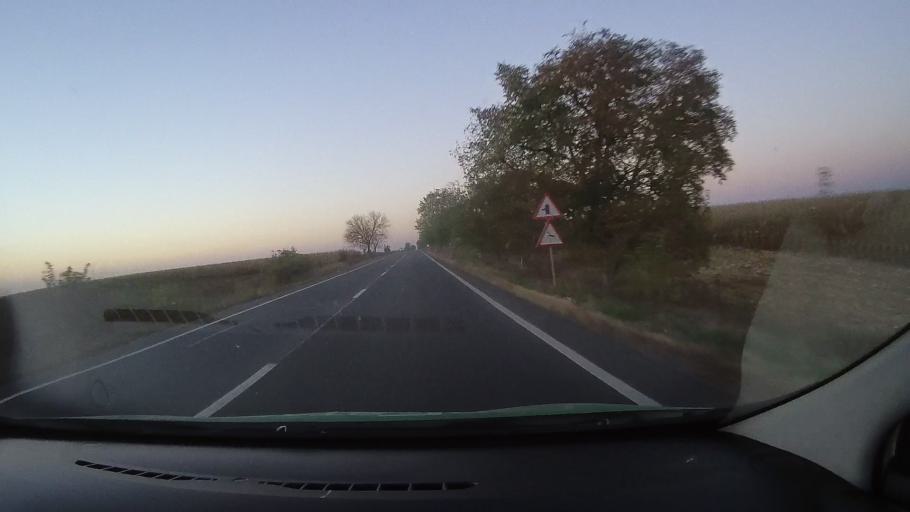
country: RO
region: Bihor
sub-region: Comuna Tarcea
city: Tarcea
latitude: 47.4713
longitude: 22.1651
